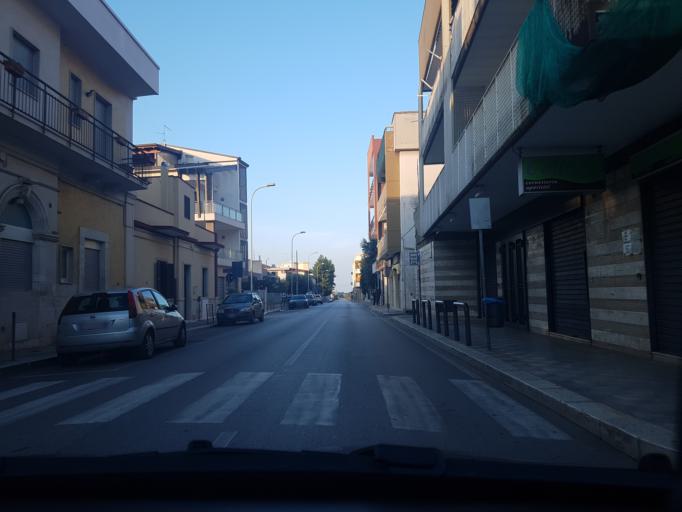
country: IT
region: Apulia
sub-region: Provincia di Bari
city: Bitritto
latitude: 41.0449
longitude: 16.8270
